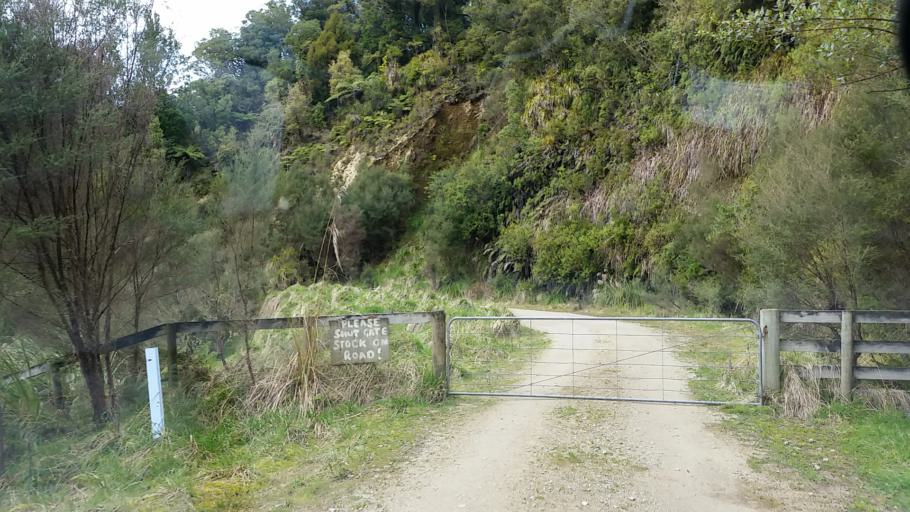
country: NZ
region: Taranaki
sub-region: South Taranaki District
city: Patea
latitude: -39.5840
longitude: 174.6816
